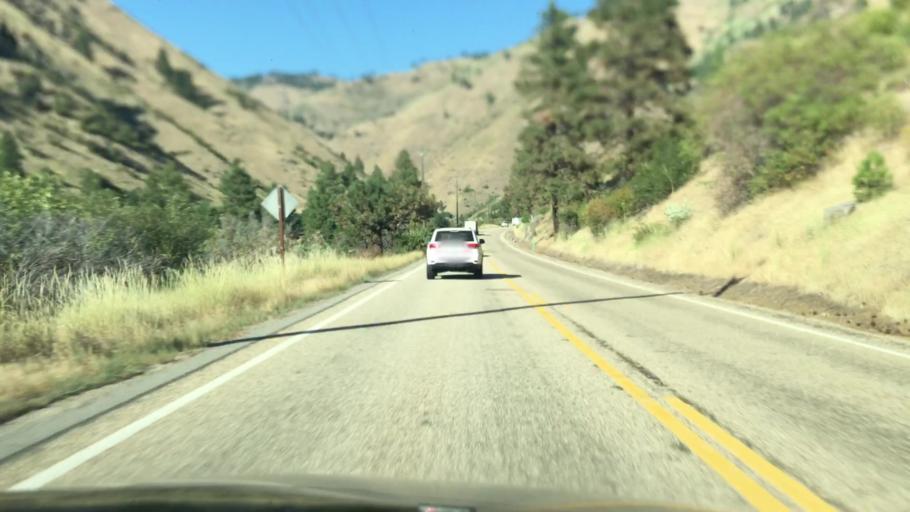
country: US
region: Idaho
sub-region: Boise County
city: Idaho City
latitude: 44.0227
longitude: -116.1480
